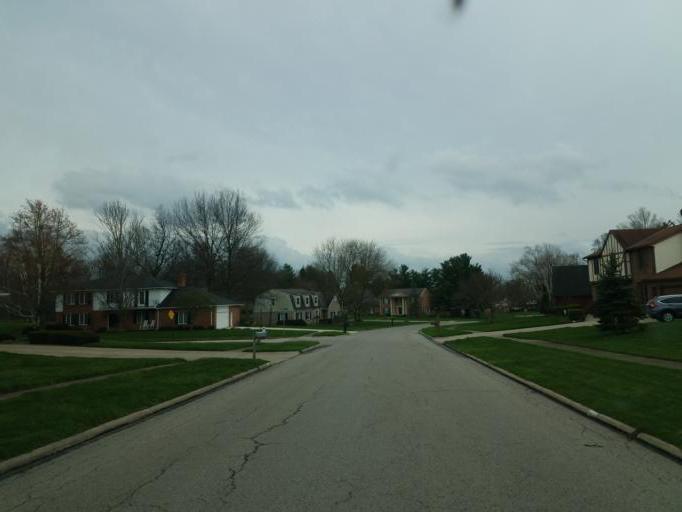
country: US
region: Ohio
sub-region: Richland County
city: Lexington
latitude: 40.7190
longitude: -82.5570
